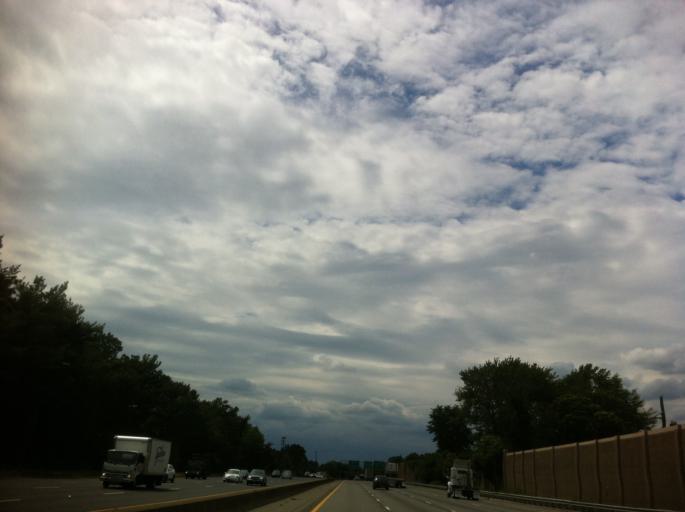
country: US
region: New Jersey
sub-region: Passaic County
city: Paterson
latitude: 40.9086
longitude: -74.1746
